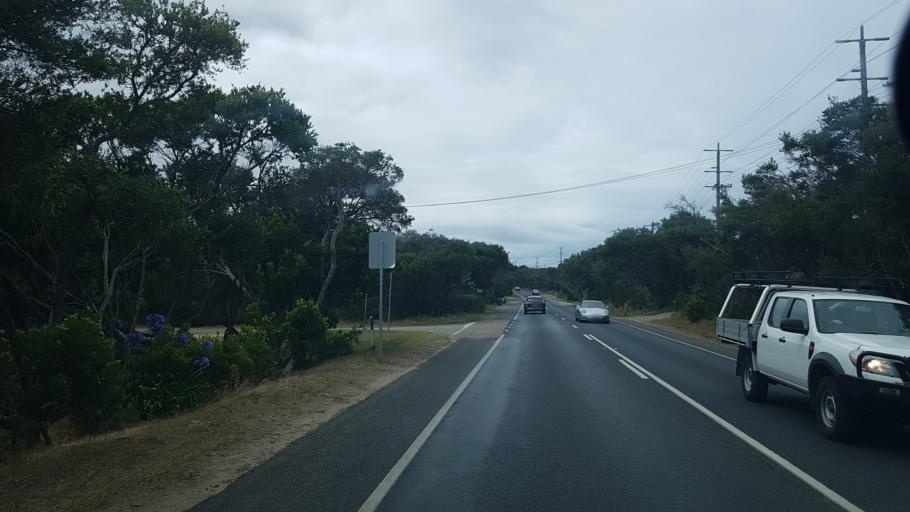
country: AU
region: Victoria
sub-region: Mornington Peninsula
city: Blairgowrie
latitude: -38.3649
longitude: 144.7657
